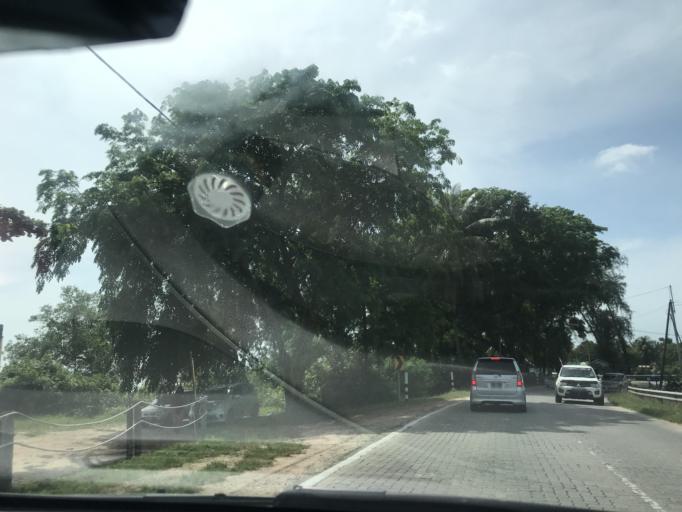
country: MY
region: Kelantan
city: Tumpat
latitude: 6.2072
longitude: 102.1431
